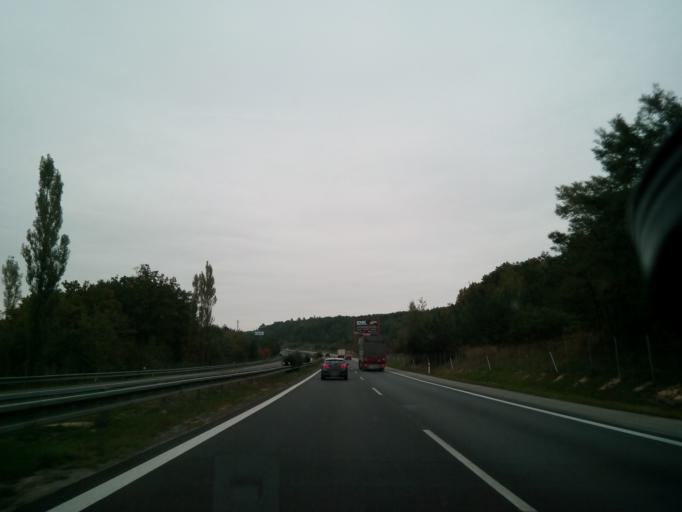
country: SK
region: Kosicky
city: Kosice
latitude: 48.7638
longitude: 21.2887
